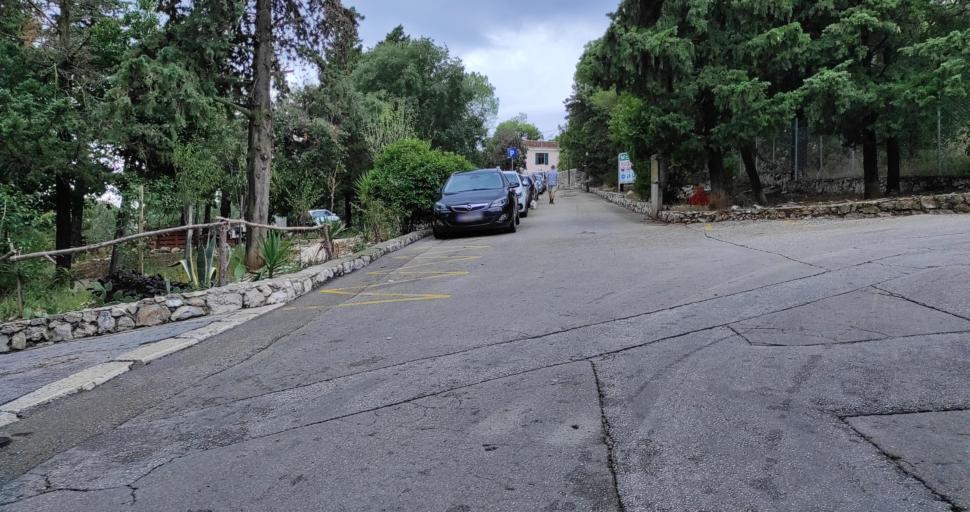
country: HR
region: Splitsko-Dalmatinska
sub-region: Grad Split
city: Split
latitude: 43.5088
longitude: 16.4306
